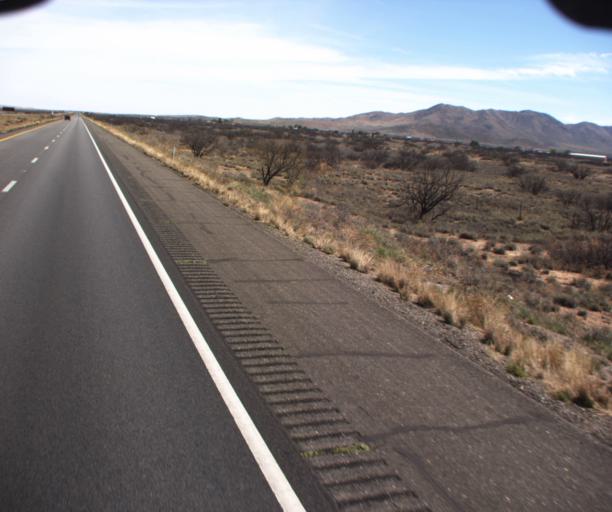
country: US
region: Arizona
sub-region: Cochise County
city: Willcox
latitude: 32.2882
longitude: -109.8206
